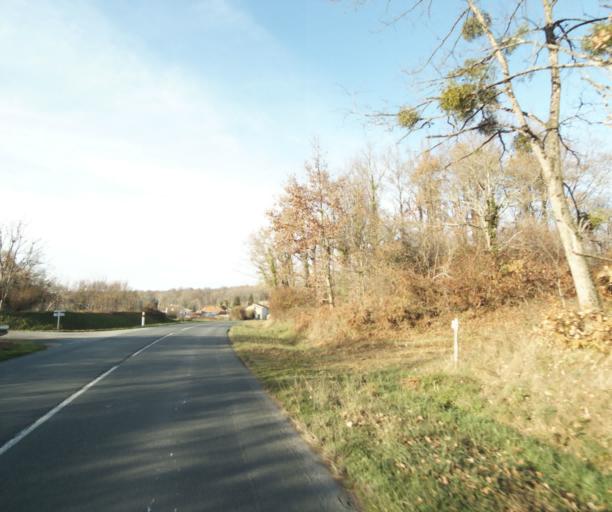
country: FR
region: Poitou-Charentes
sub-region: Departement de la Charente-Maritime
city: Burie
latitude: 45.7935
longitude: -0.4396
